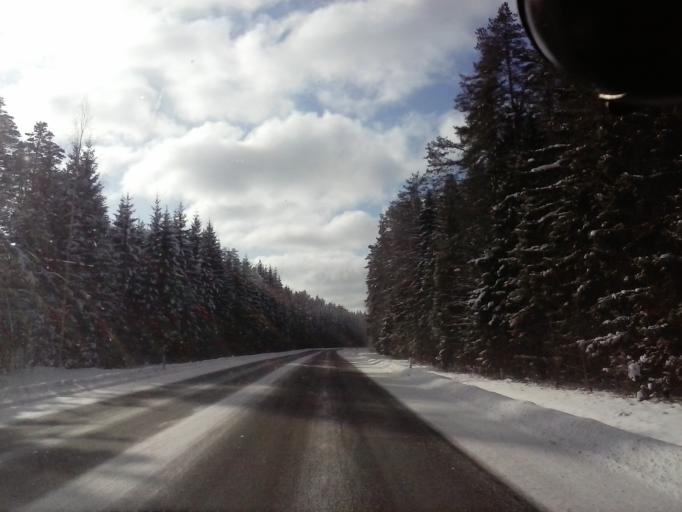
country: EE
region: Viljandimaa
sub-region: Moisakuela linn
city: Moisakula
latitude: 58.2250
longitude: 25.1071
